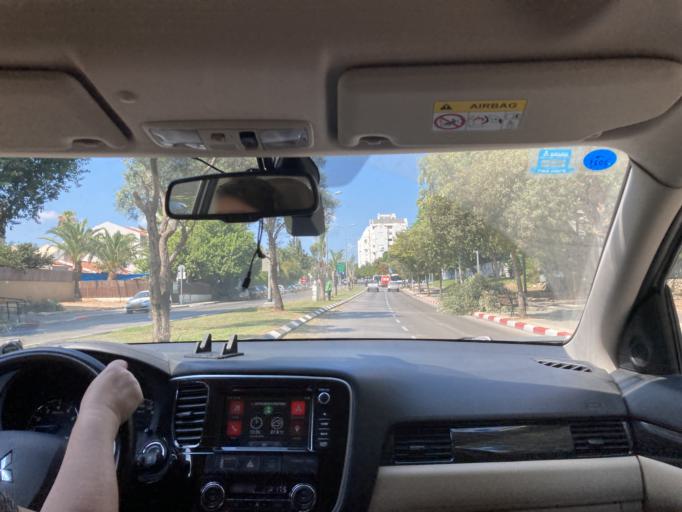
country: IL
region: Tel Aviv
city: Ramat HaSharon
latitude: 32.1147
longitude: 34.8396
